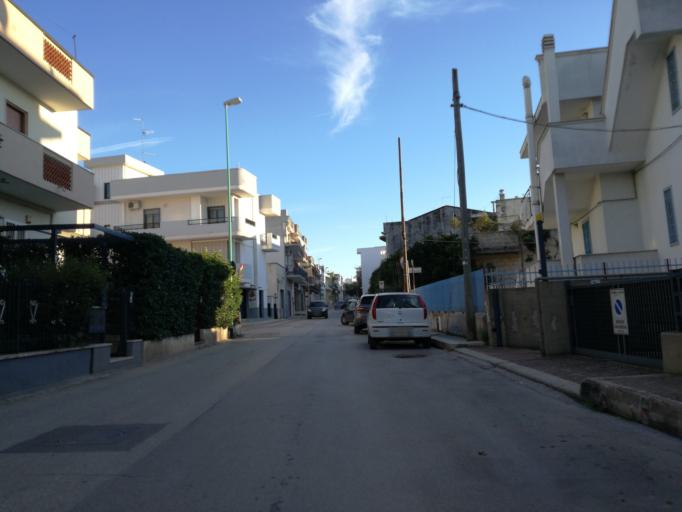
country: IT
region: Apulia
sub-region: Provincia di Bari
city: Adelfia
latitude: 41.0066
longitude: 16.8637
